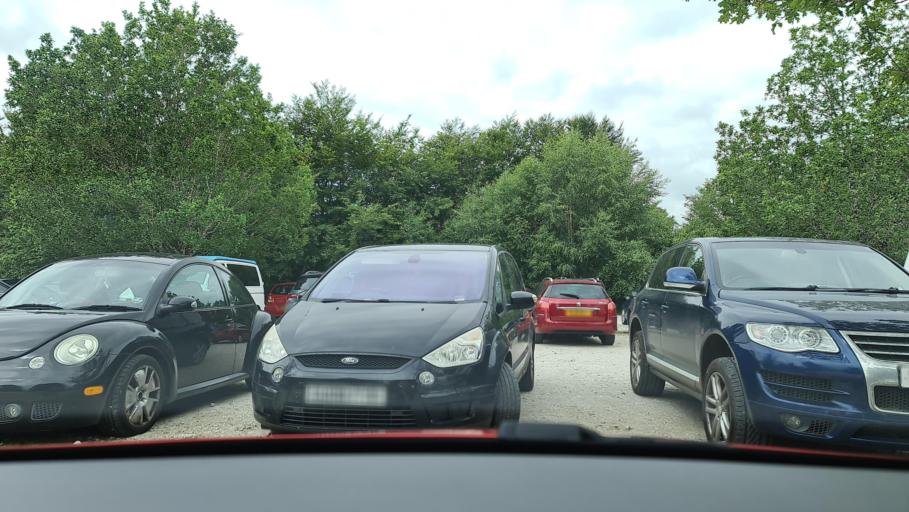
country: GB
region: England
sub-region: Cornwall
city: Bodmin
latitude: 50.4470
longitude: -4.6948
